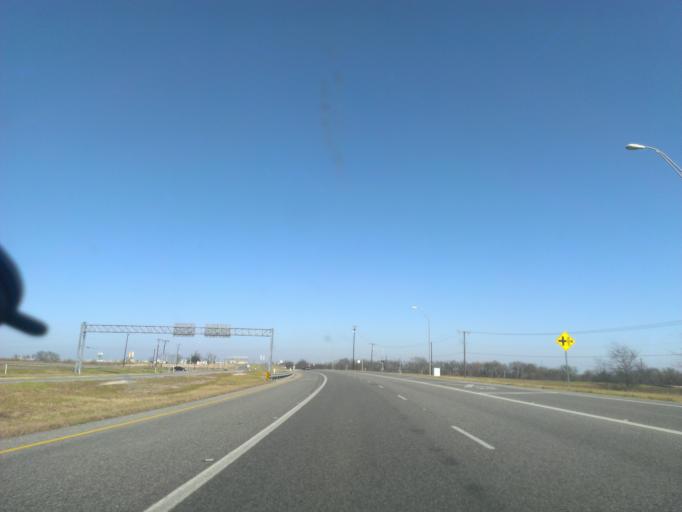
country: US
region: Texas
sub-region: Williamson County
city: Taylor
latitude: 30.5740
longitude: -97.3775
